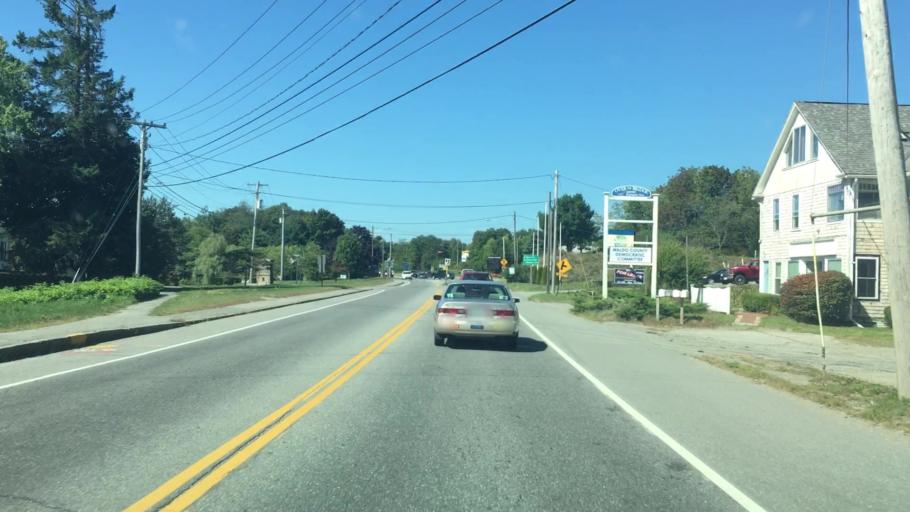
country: US
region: Maine
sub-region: Waldo County
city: Belfast
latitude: 44.4341
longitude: -69.0024
